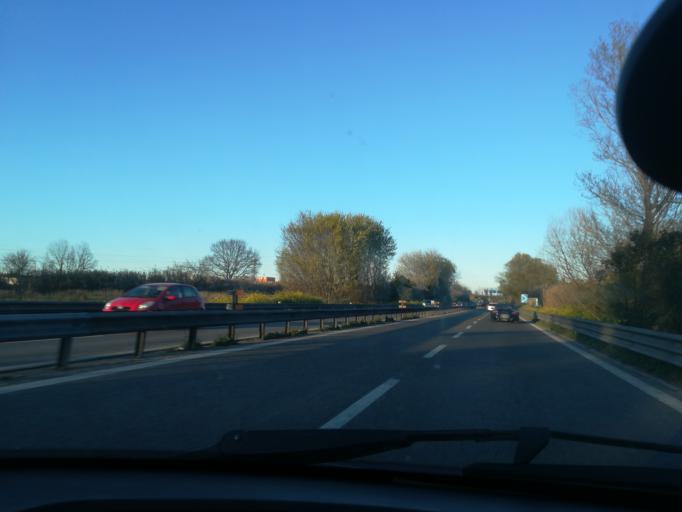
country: IT
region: The Marches
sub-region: Provincia di Macerata
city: Santa Maria Apparente
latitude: 43.2863
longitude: 13.7026
